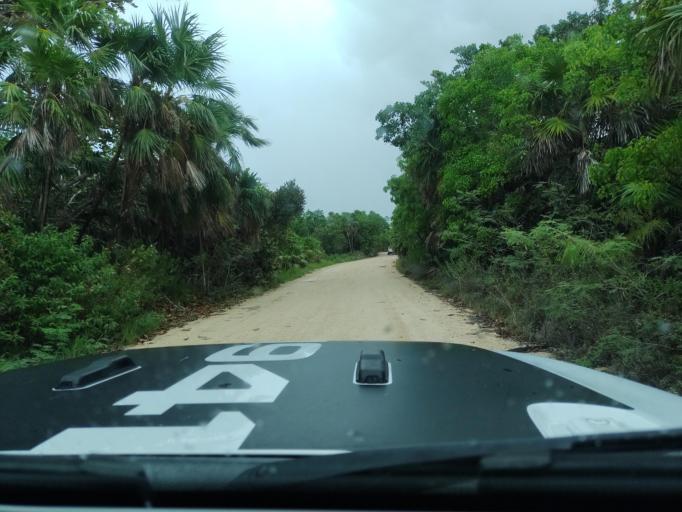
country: MX
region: Quintana Roo
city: Tulum
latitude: 20.0565
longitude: -87.4810
